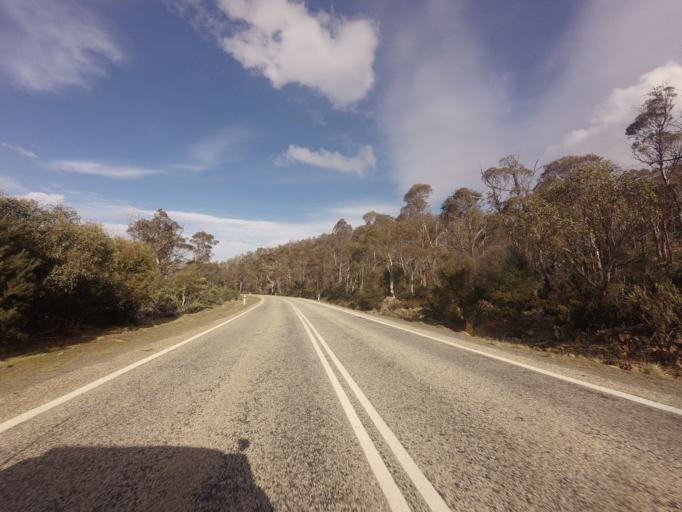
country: AU
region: Tasmania
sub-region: Meander Valley
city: Deloraine
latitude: -41.9881
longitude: 146.6800
